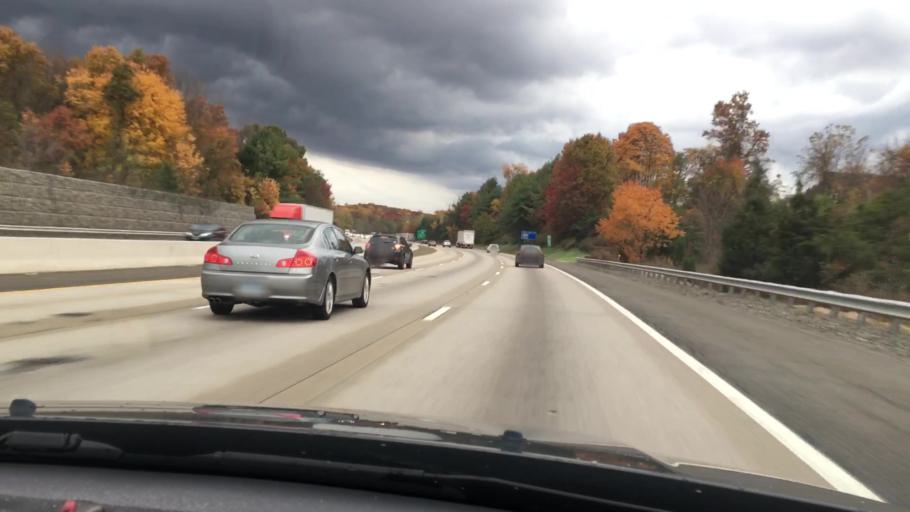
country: US
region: New Jersey
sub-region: Morris County
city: Lincoln Park
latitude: 40.9321
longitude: -74.3568
